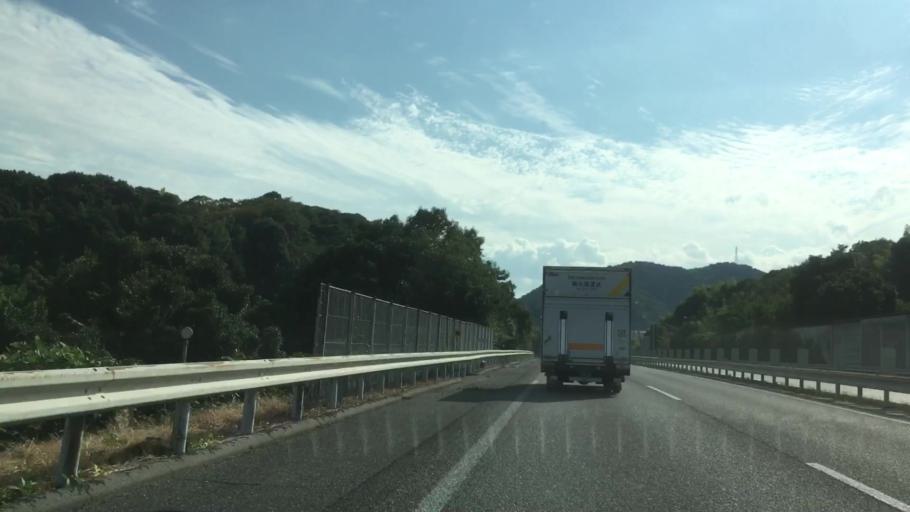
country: JP
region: Yamaguchi
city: Otake
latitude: 34.2444
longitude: 132.2169
